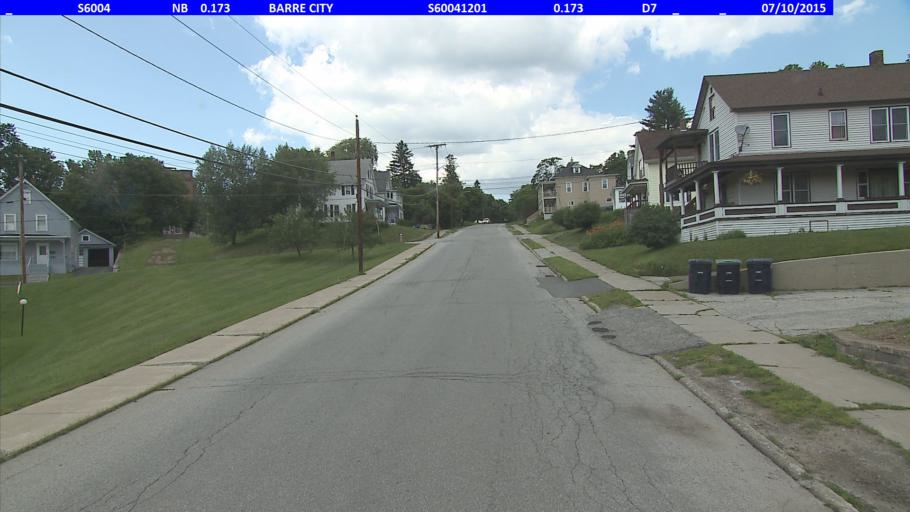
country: US
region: Vermont
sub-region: Washington County
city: Barre
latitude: 44.2082
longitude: -72.5113
